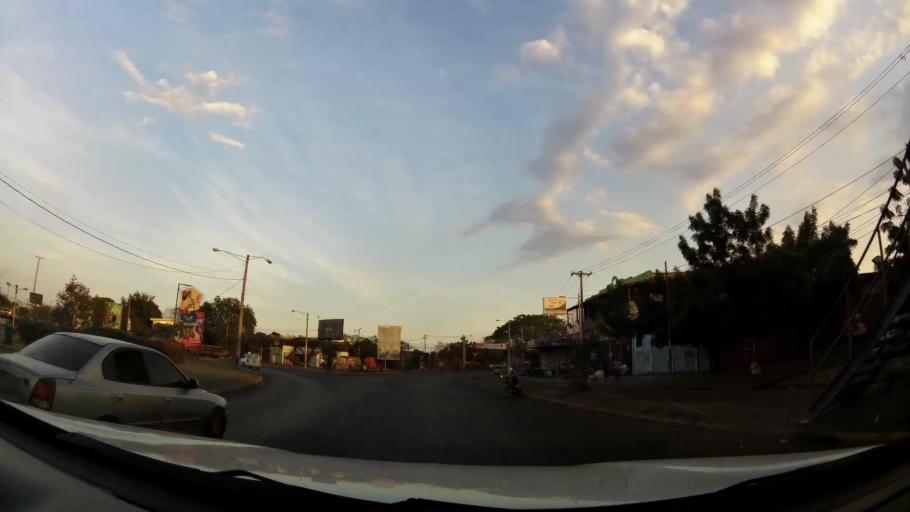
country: NI
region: Managua
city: Managua
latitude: 12.1427
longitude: -86.2253
